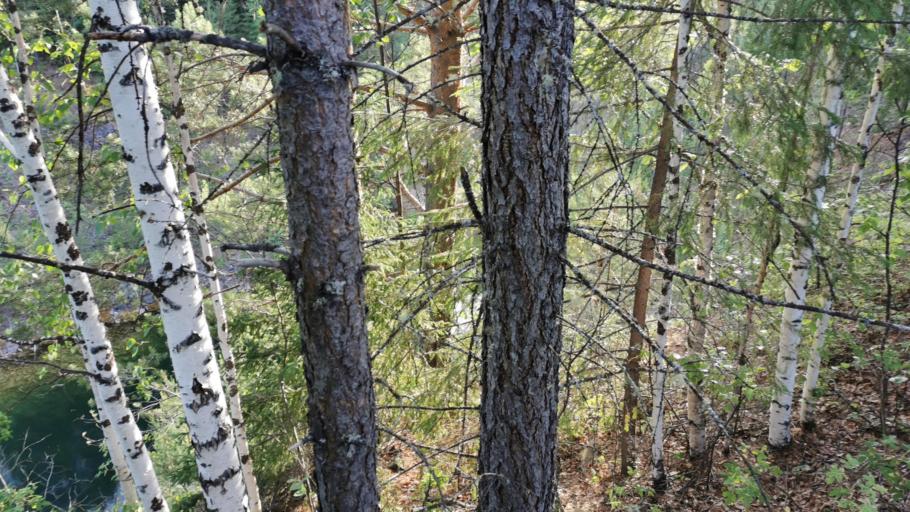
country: RU
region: Sverdlovsk
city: Karpinsk
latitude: 59.5588
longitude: 60.0133
